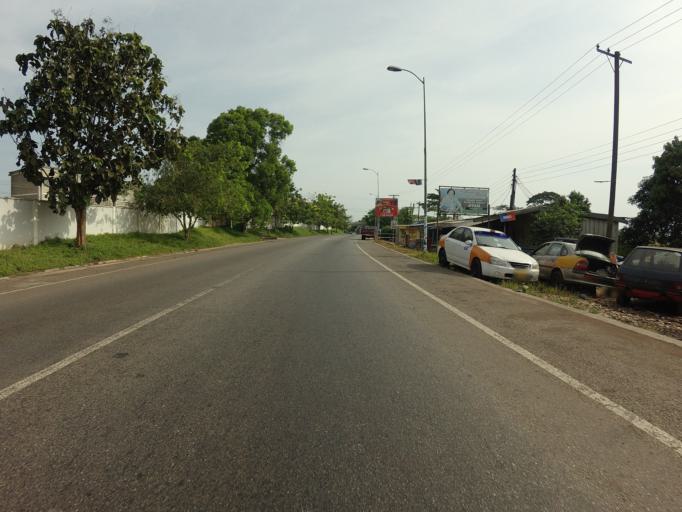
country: GH
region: Eastern
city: Aburi
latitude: 5.8371
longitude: -0.1780
